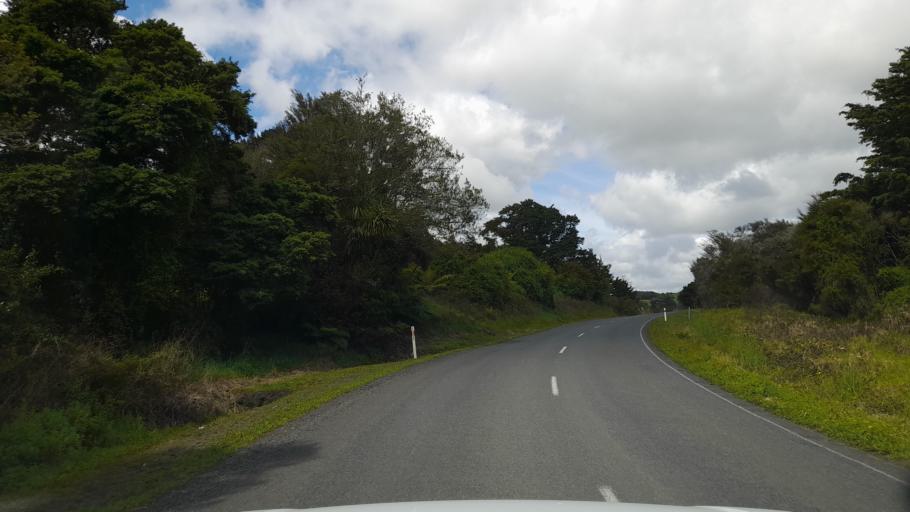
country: NZ
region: Northland
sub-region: Whangarei
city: Maungatapere
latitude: -35.6513
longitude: 174.1454
